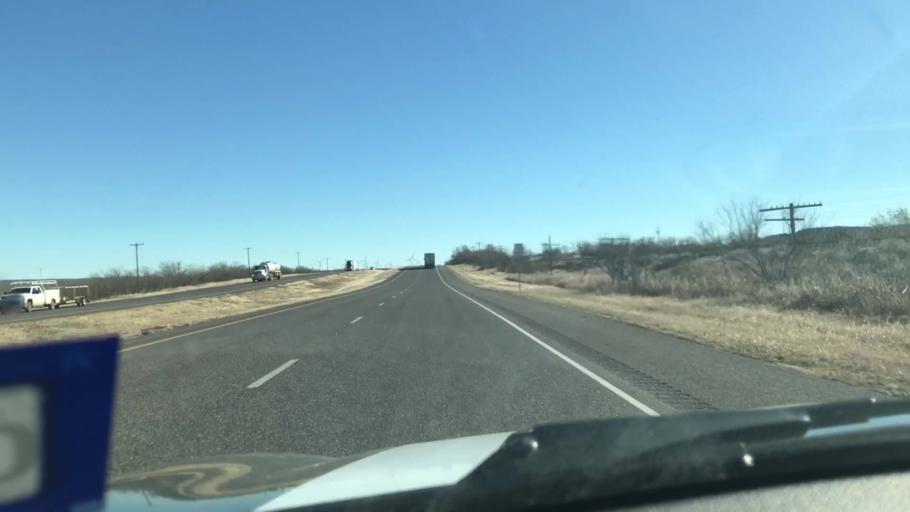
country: US
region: Texas
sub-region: Scurry County
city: Snyder
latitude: 32.9581
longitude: -101.0896
